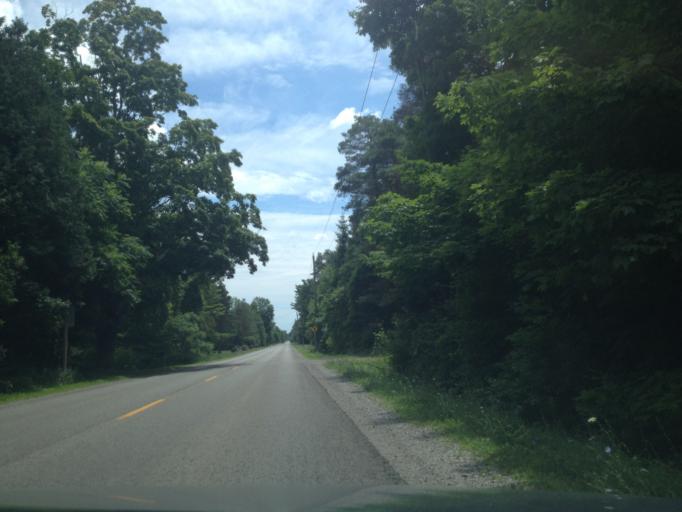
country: CA
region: Ontario
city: Norfolk County
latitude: 42.8064
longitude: -80.3175
